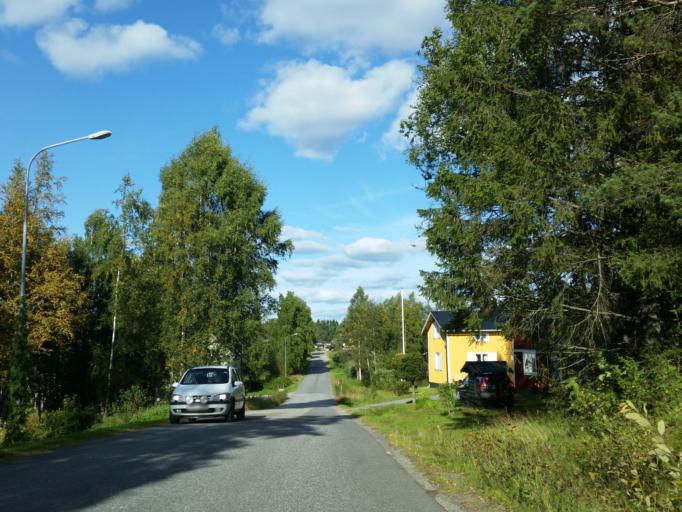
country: SE
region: Vaesterbotten
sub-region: Robertsfors Kommun
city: Robertsfors
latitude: 64.1683
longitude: 20.9351
